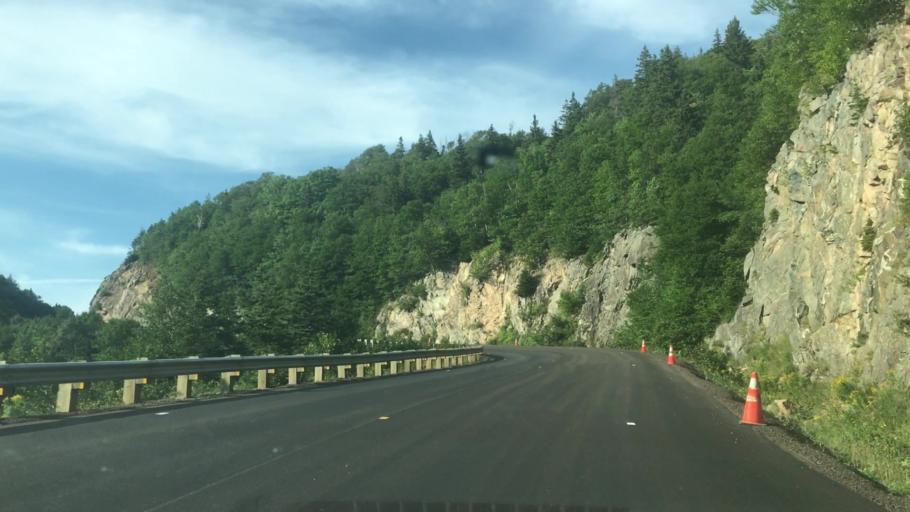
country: CA
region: Nova Scotia
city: Sydney Mines
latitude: 46.8192
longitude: -60.6527
